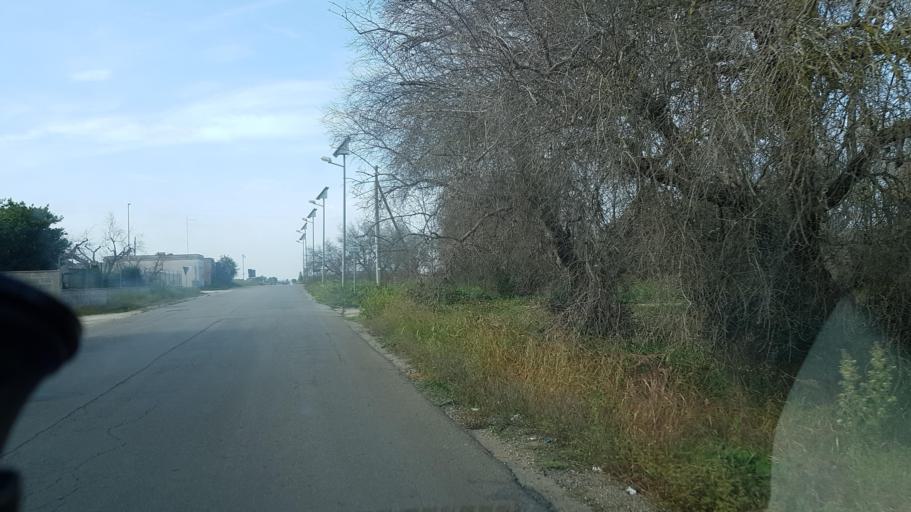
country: IT
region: Apulia
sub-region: Provincia di Brindisi
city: San Donaci
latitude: 40.4441
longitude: 17.9129
